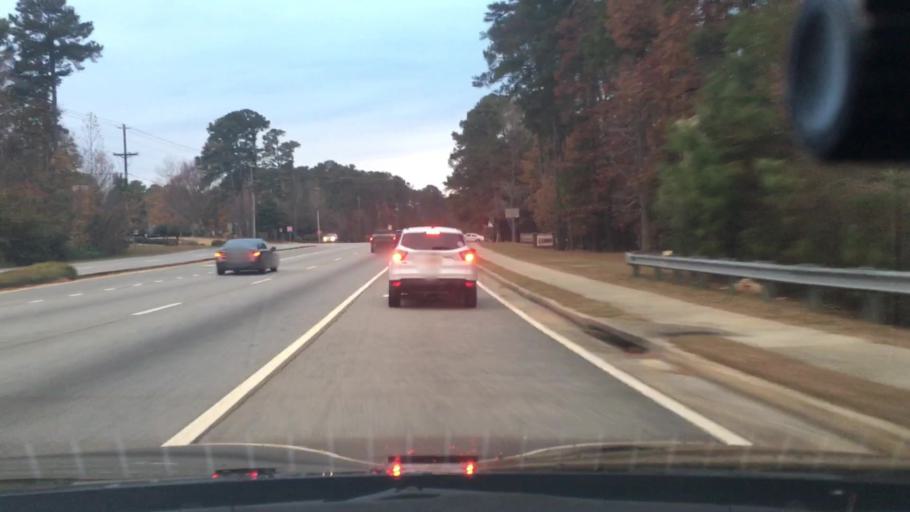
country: US
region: Georgia
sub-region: Fayette County
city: Peachtree City
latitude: 33.3995
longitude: -84.5944
